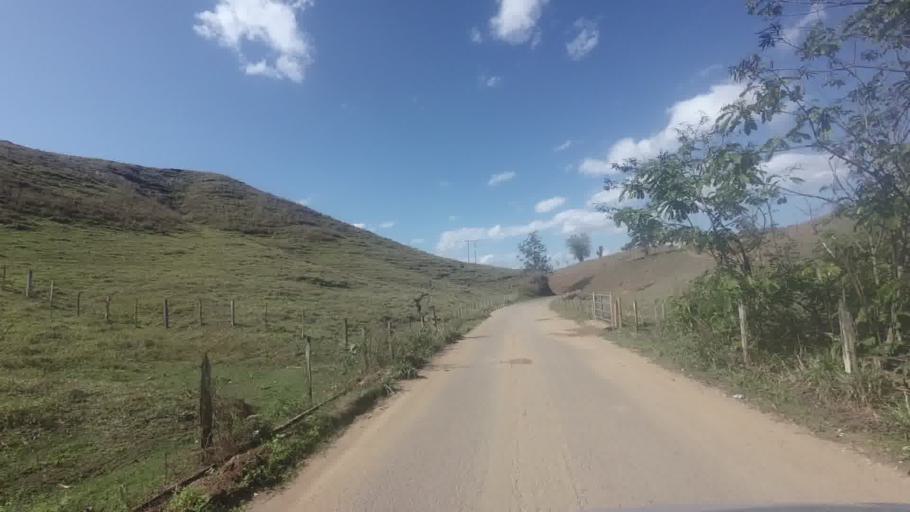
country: BR
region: Rio de Janeiro
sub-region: Bom Jesus Do Itabapoana
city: Bom Jesus do Itabapoana
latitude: -21.1102
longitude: -41.6488
